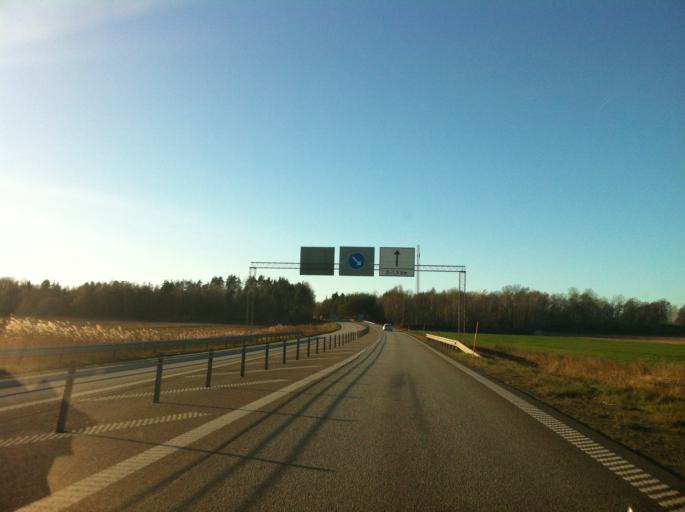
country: SE
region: Blekinge
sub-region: Karlshamns Kommun
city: Morrum
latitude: 56.1785
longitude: 14.7479
